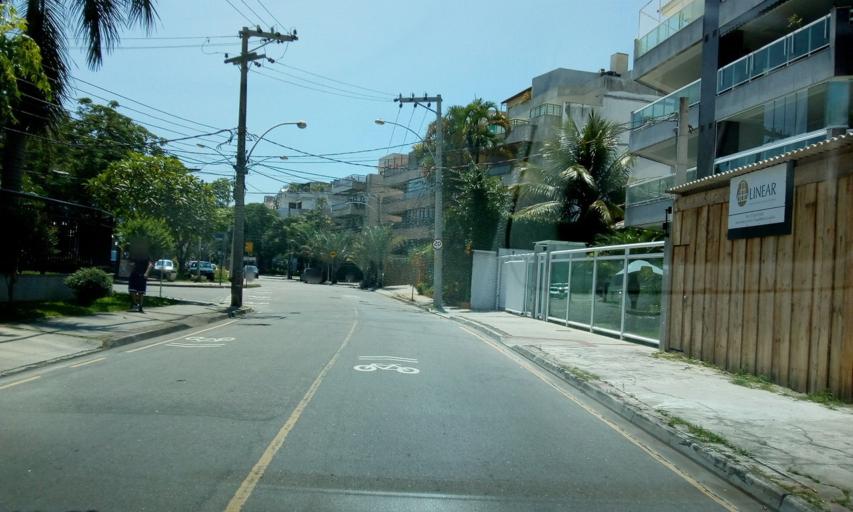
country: BR
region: Rio de Janeiro
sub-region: Nilopolis
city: Nilopolis
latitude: -23.0223
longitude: -43.4642
